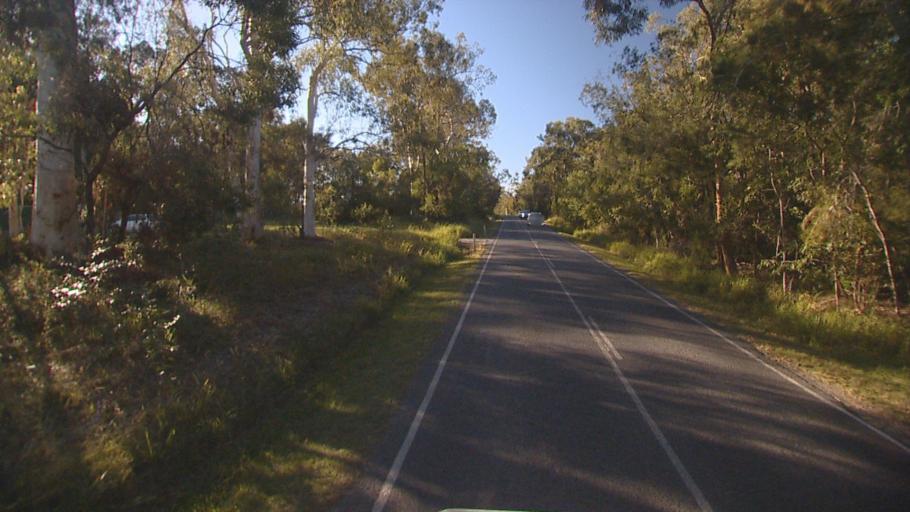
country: AU
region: Queensland
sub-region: Logan
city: Logan Reserve
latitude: -27.7282
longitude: 153.0897
